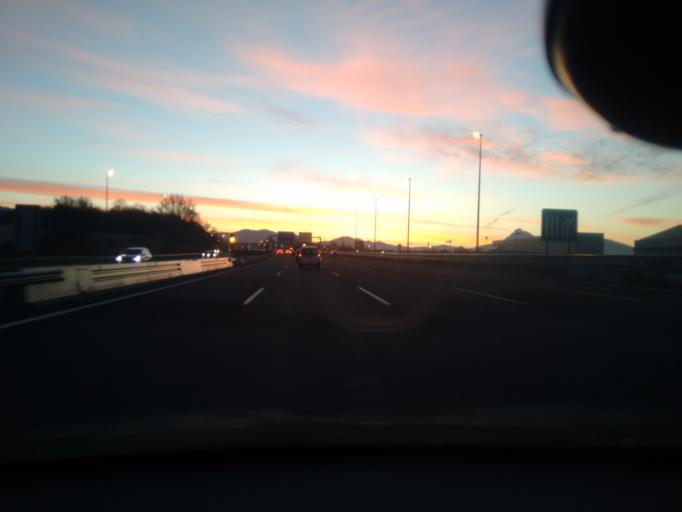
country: ES
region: Basque Country
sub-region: Bizkaia
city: Iurreta
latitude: 43.1810
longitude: -2.6481
